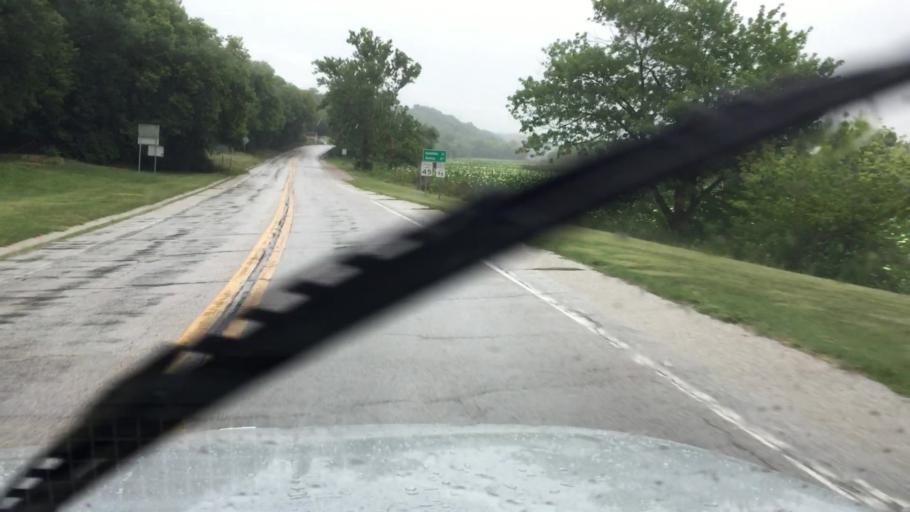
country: US
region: Illinois
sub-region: Hancock County
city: Nauvoo
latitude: 40.5386
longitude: -91.3848
